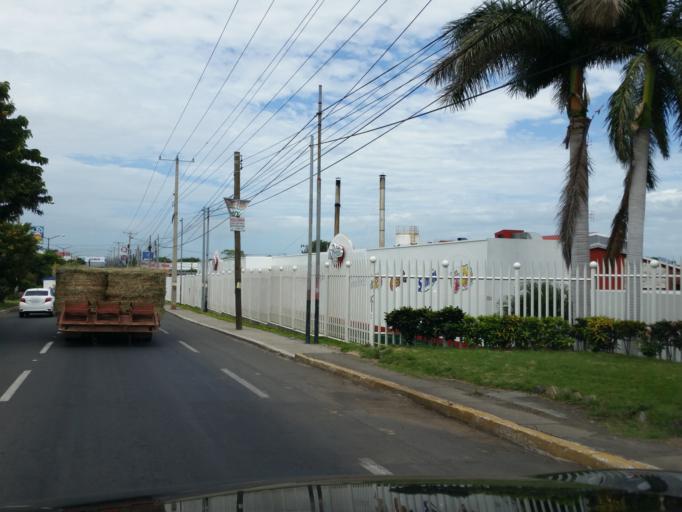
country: NI
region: Managua
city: Managua
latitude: 12.1511
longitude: -86.2289
